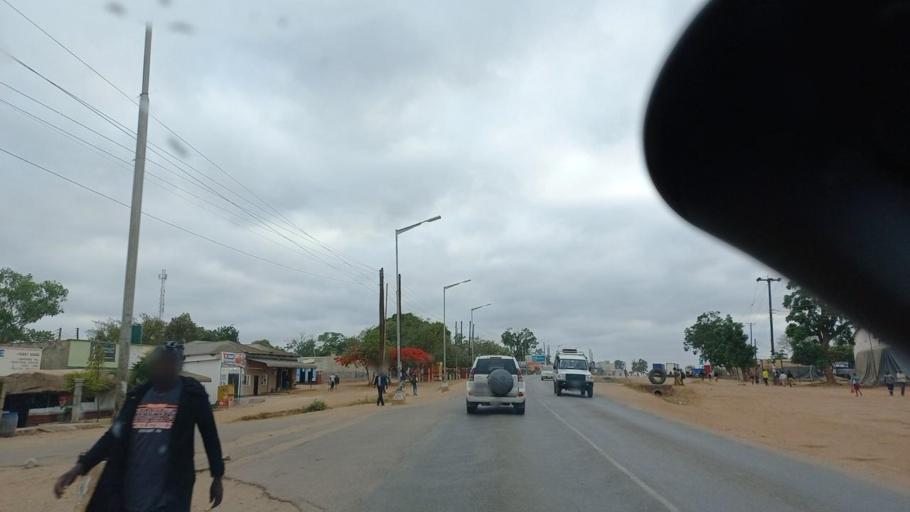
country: ZM
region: Lusaka
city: Chongwe
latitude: -15.3284
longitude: 28.6780
